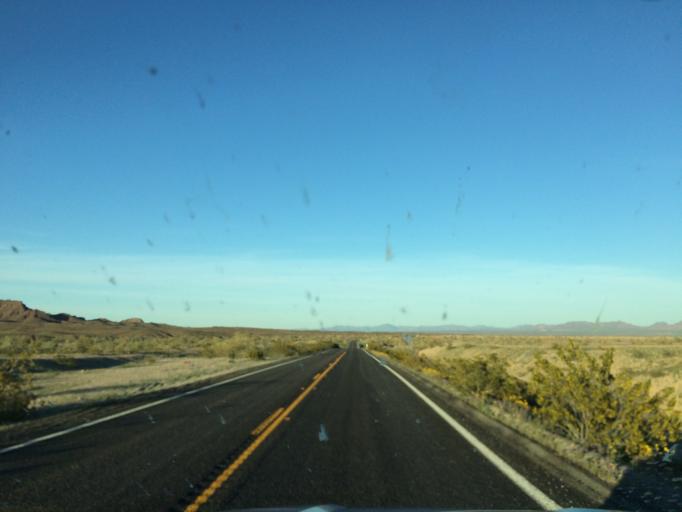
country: US
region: California
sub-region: Riverside County
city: Mesa Verde
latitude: 33.2753
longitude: -114.7894
